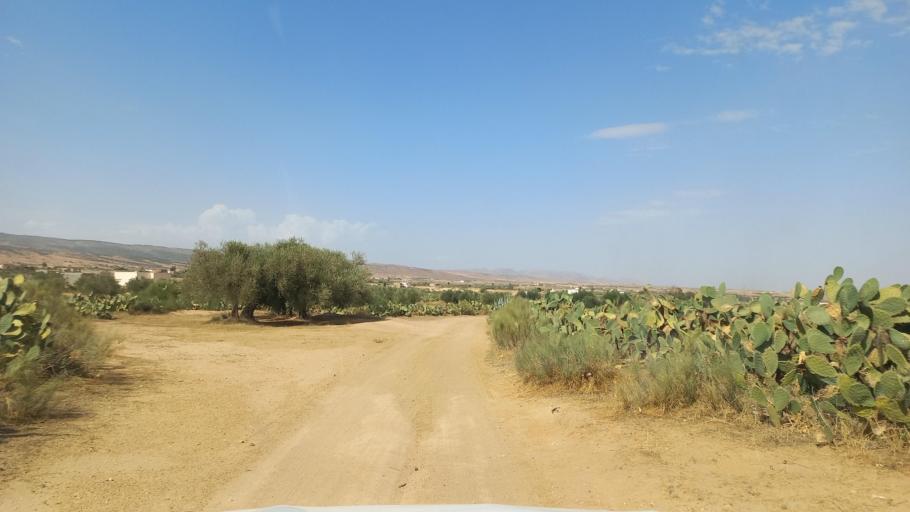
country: TN
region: Al Qasrayn
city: Kasserine
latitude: 35.2744
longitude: 8.9474
